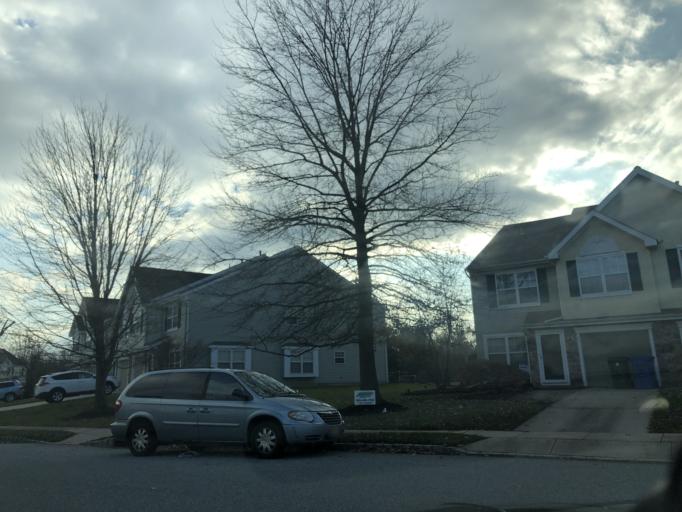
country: US
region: New Jersey
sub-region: Burlington County
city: Marlton
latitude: 39.9142
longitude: -74.9191
